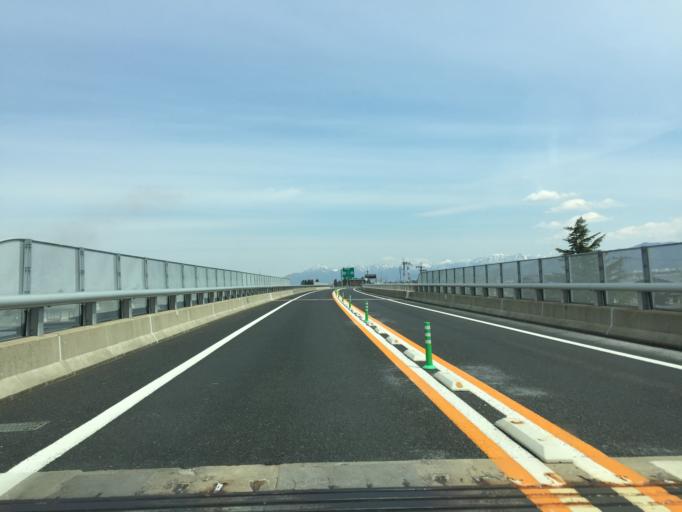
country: JP
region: Yamagata
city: Sagae
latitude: 38.2958
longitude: 140.3017
